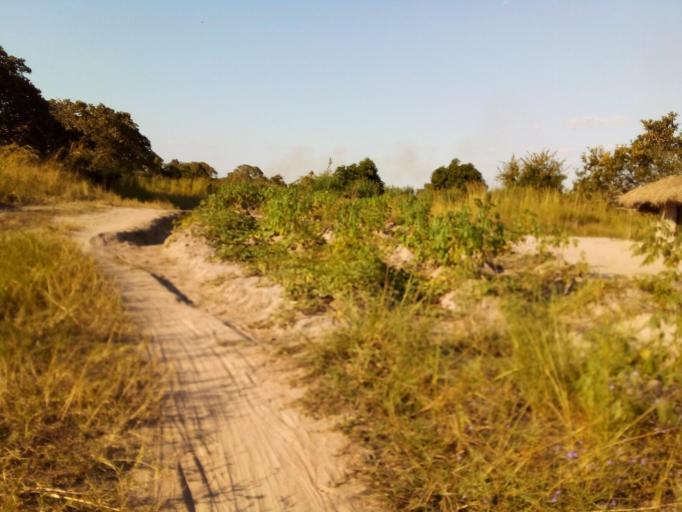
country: MZ
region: Zambezia
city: Quelimane
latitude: -17.5503
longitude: 36.7081
